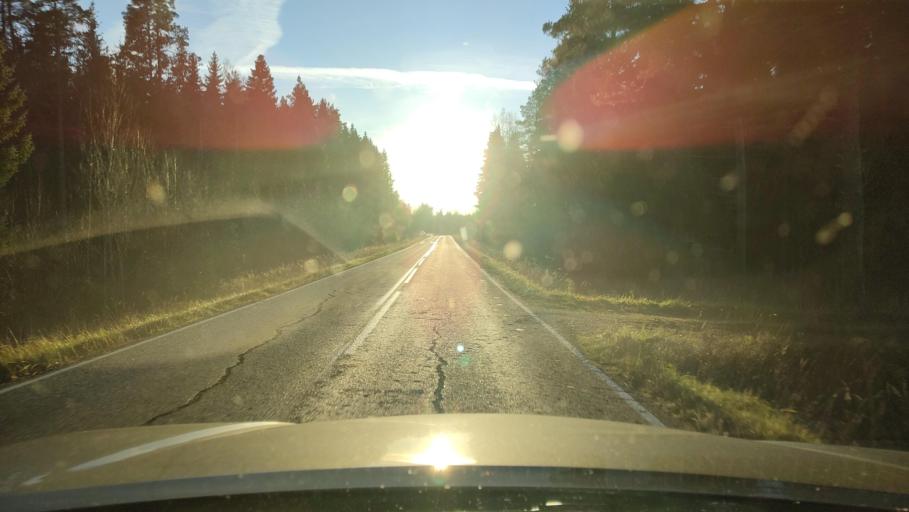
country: FI
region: Ostrobothnia
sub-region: Vaasa
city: Malax
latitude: 62.6925
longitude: 21.5591
